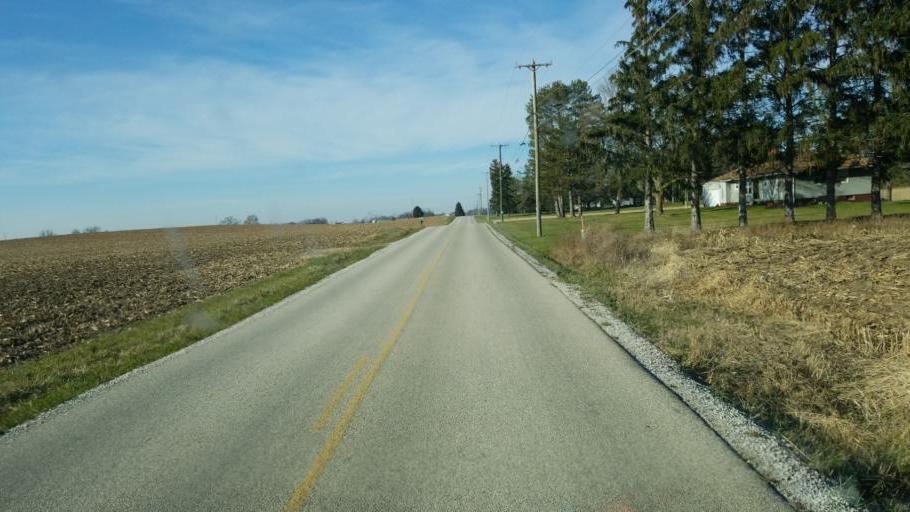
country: US
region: Ohio
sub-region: Richland County
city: Shelby
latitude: 40.8431
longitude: -82.6449
